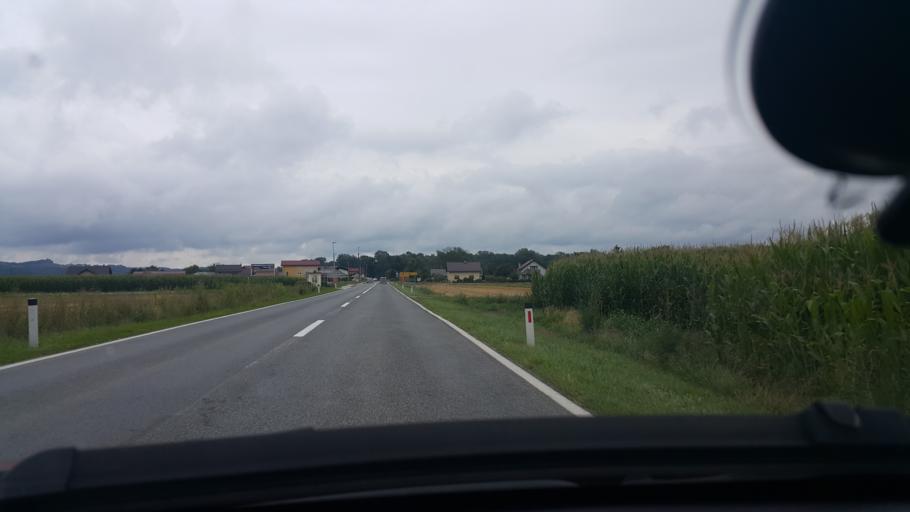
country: SI
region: Zavrc
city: Zavrc
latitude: 46.4142
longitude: 16.0611
